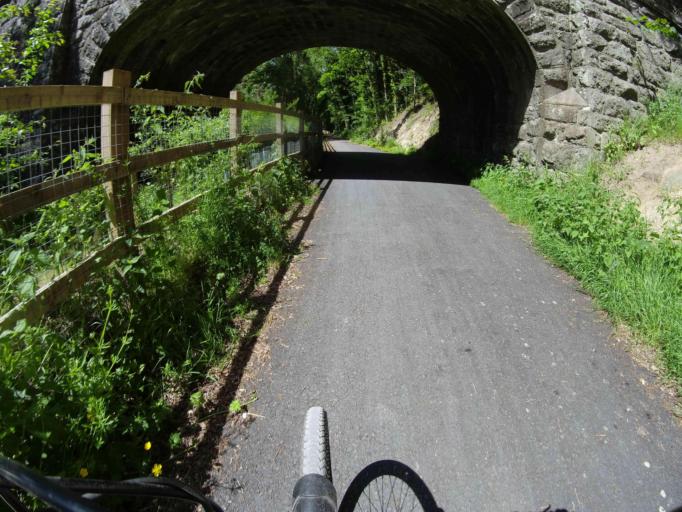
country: GB
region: England
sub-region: Devon
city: Bovey Tracey
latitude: 50.6479
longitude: -3.7420
